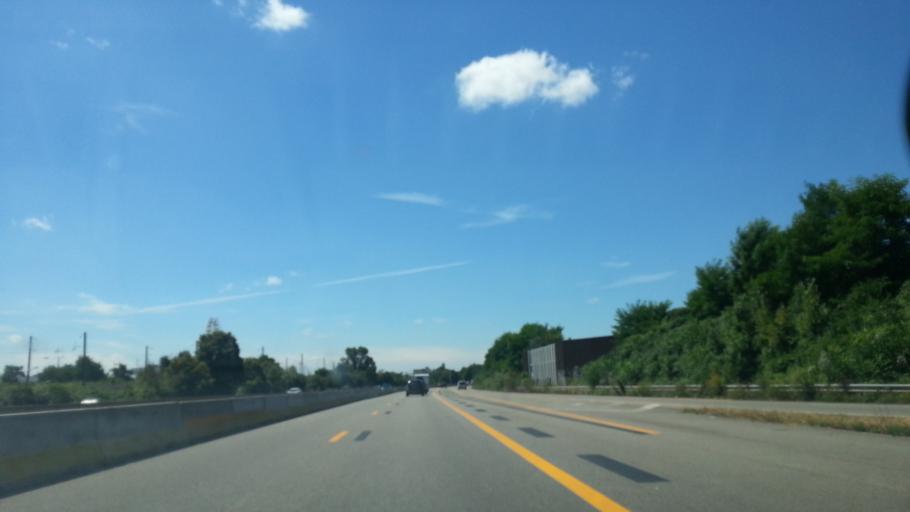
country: FR
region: Alsace
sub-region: Departement du Haut-Rhin
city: Illzach
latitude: 47.7687
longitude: 7.3388
